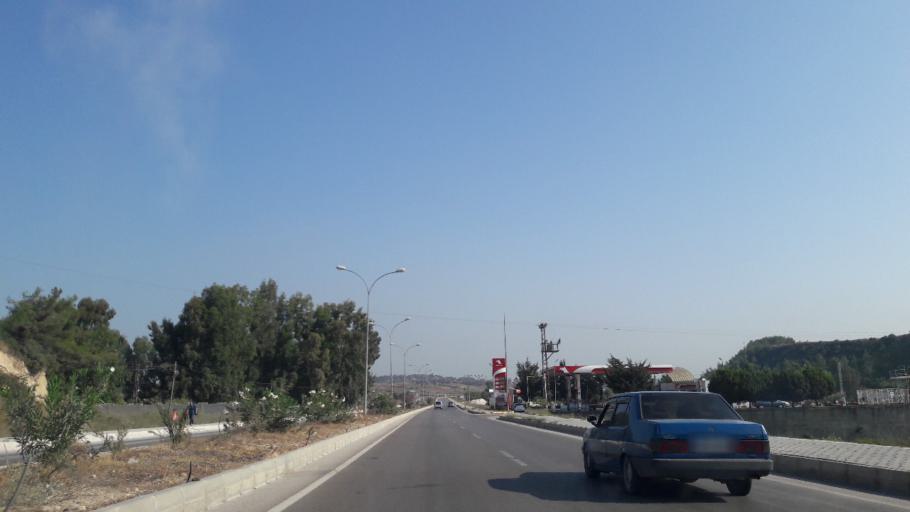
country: TR
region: Adana
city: Yuregir
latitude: 37.0545
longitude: 35.4412
